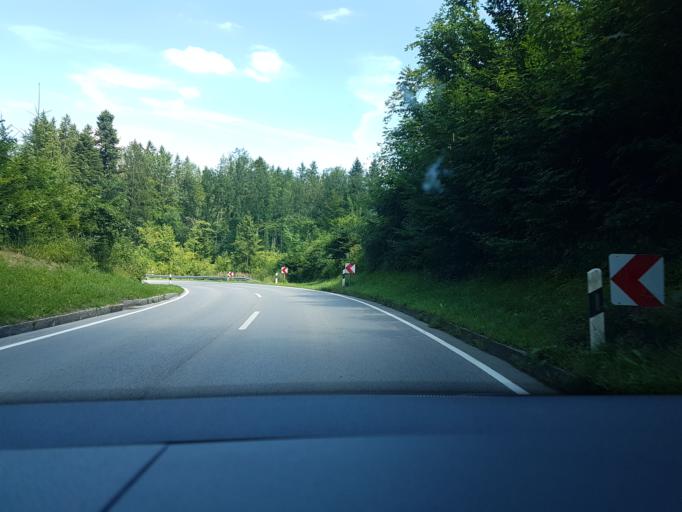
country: DE
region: Bavaria
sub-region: Upper Bavaria
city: Samerberg
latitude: 47.7921
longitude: 12.1994
